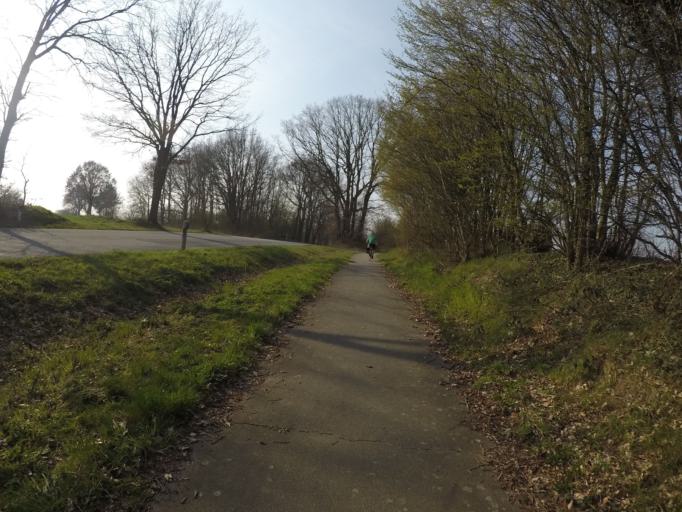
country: DE
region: Schleswig-Holstein
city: Kukels
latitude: 53.9117
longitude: 10.2271
